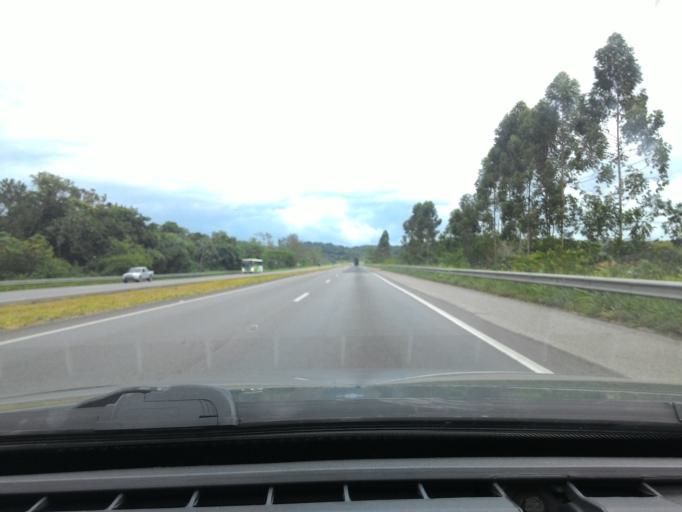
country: BR
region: Sao Paulo
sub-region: Registro
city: Registro
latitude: -24.5917
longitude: -47.8796
